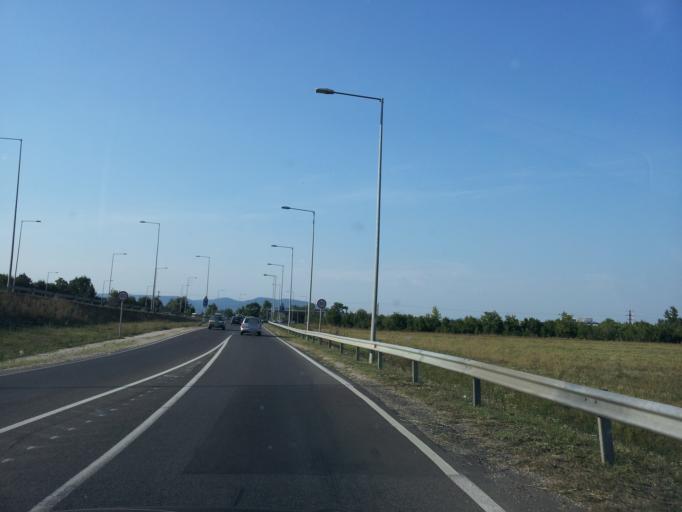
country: HU
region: Pest
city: Budakalasz
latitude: 47.6133
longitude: 19.0656
